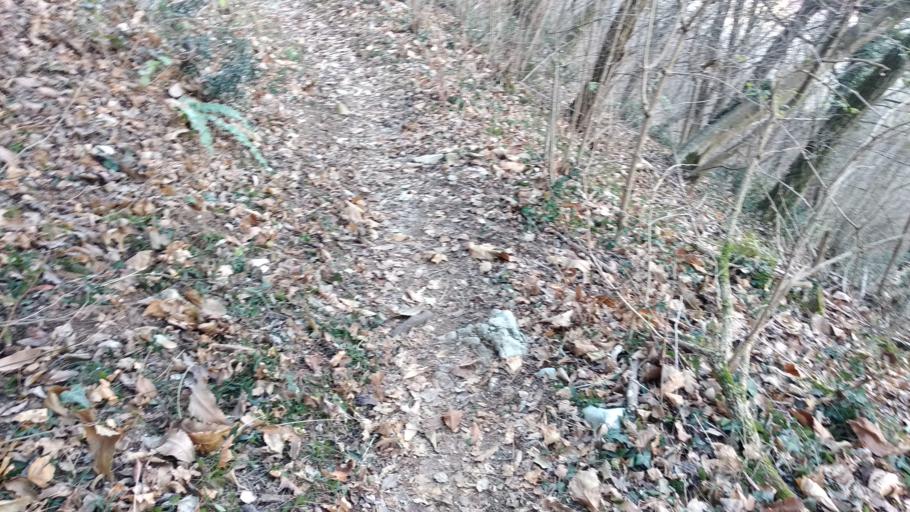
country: IT
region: Veneto
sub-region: Provincia di Vicenza
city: Schio
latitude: 45.6974
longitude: 11.3544
